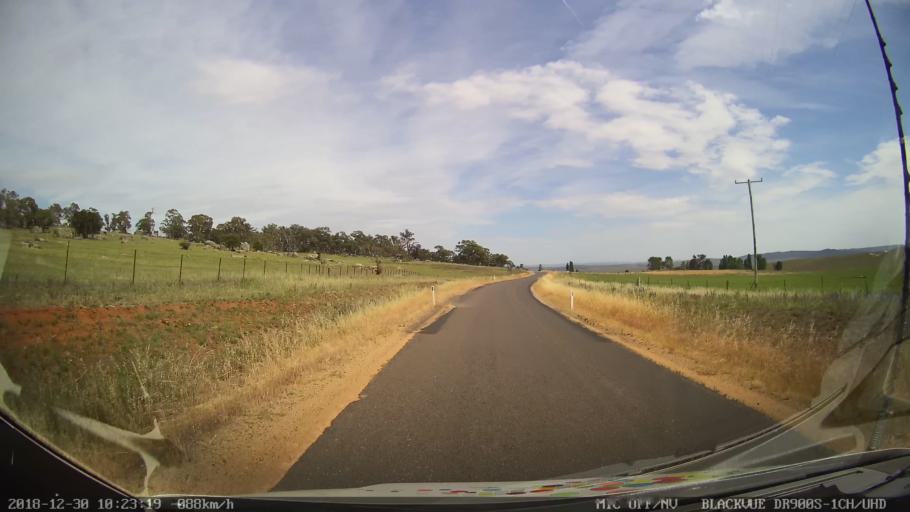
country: AU
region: New South Wales
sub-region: Snowy River
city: Berridale
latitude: -36.5390
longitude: 148.9830
